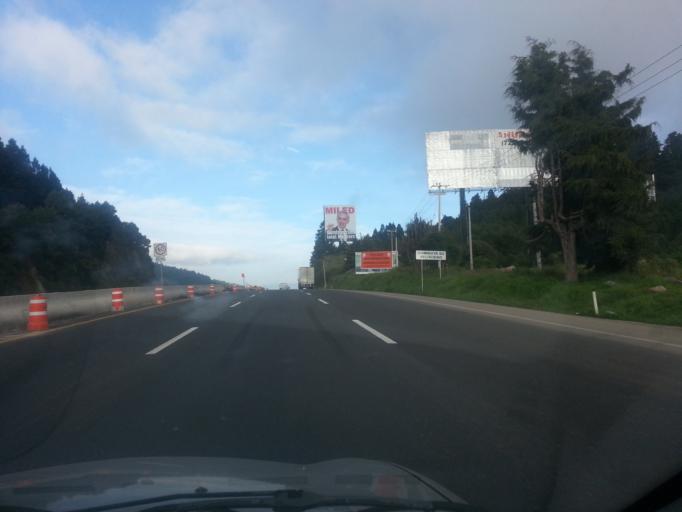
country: MX
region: Morelos
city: San Jeronimo Acazulco
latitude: 19.2991
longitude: -99.3924
